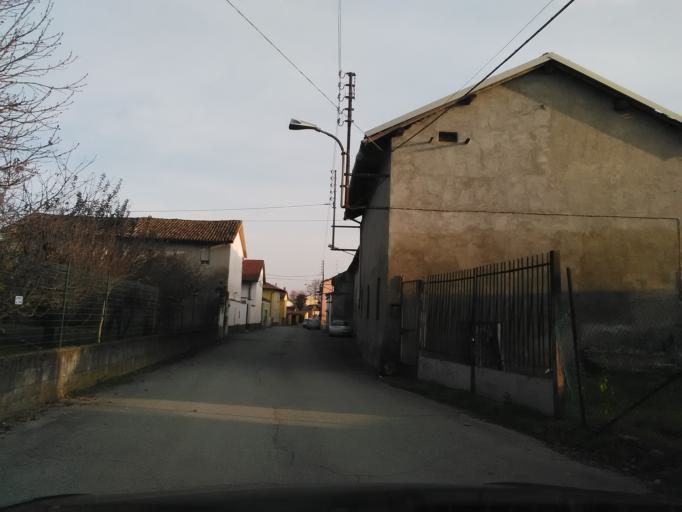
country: IT
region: Piedmont
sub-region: Provincia di Vercelli
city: Olcenengo
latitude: 45.3475
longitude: 8.2907
